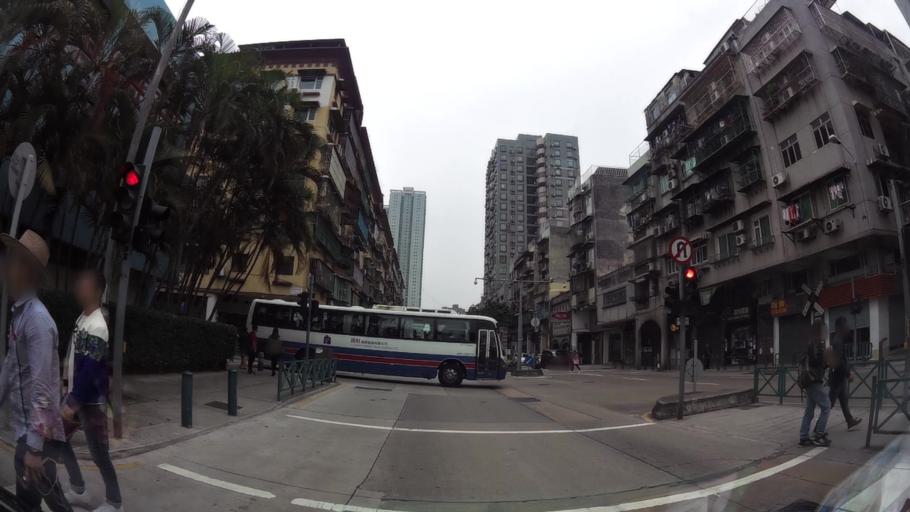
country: CN
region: Guangdong
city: Wanzai
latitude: 22.1873
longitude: 113.5312
